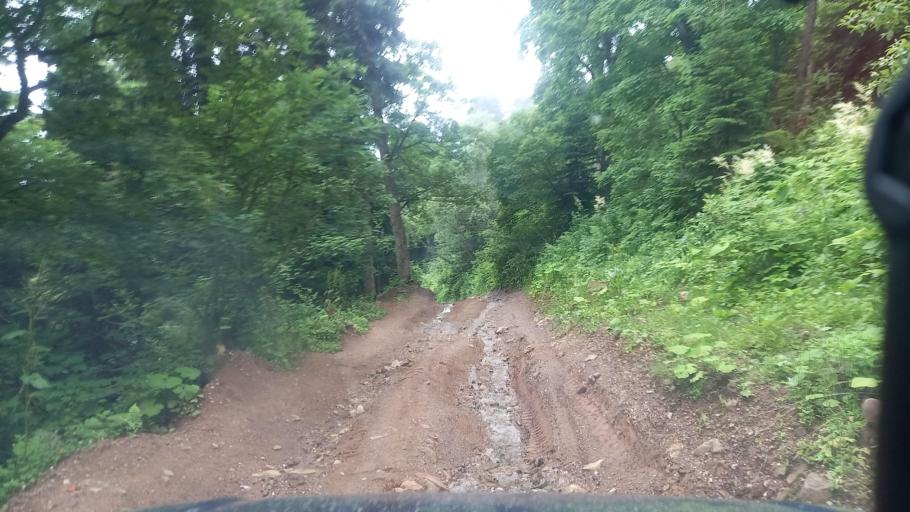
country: RU
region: Karachayevo-Cherkesiya
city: Kurdzhinovo
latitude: 43.8034
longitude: 40.8428
